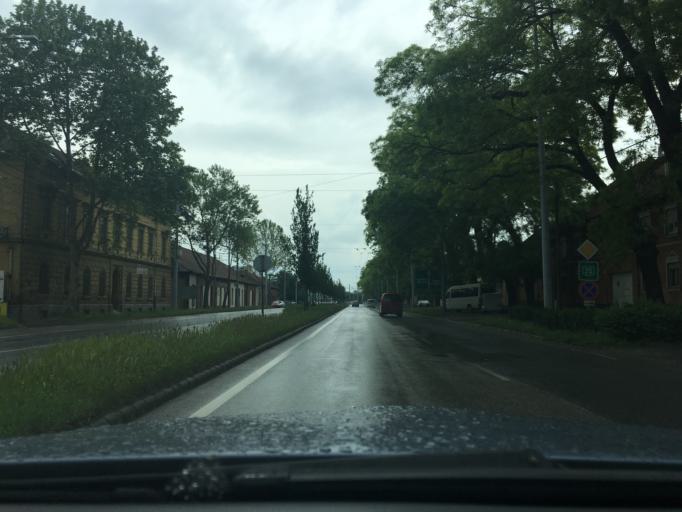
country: HU
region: Hajdu-Bihar
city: Debrecen
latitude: 47.5266
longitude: 21.6165
